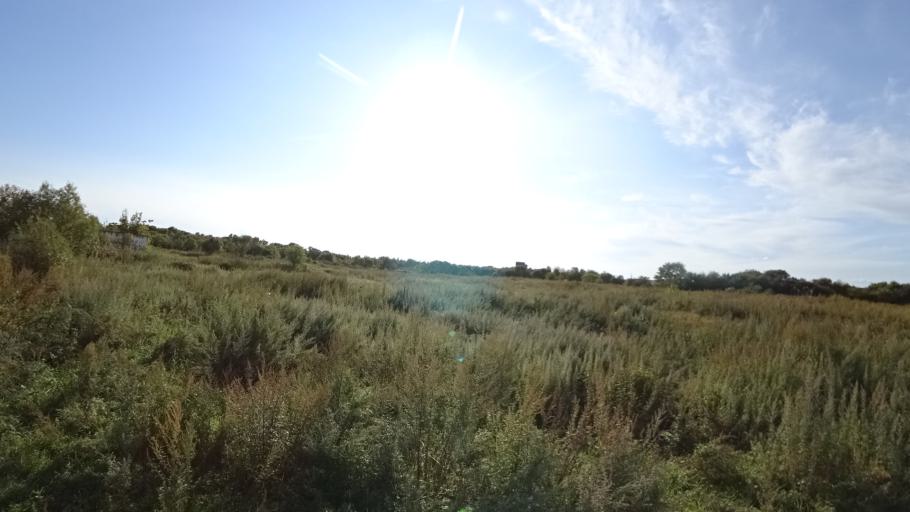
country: RU
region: Amur
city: Arkhara
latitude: 49.3488
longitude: 130.1065
